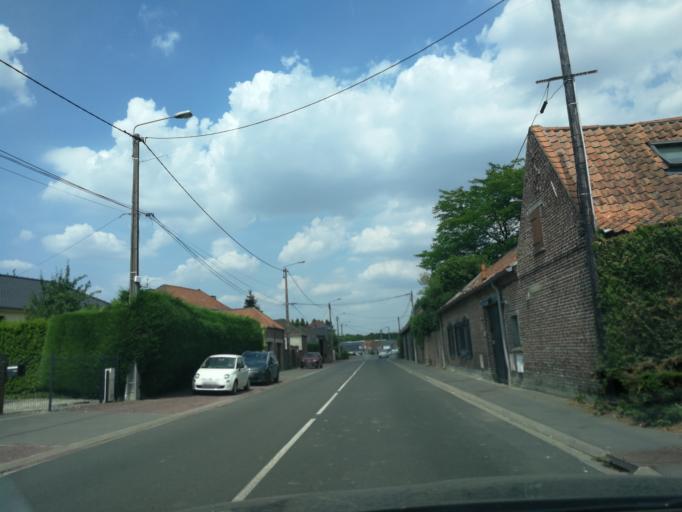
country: FR
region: Nord-Pas-de-Calais
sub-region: Departement du Nord
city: Attiches
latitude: 50.5127
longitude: 3.0604
